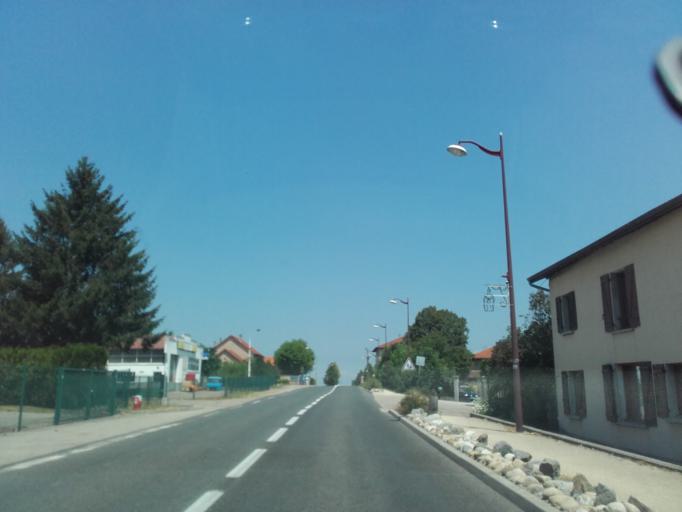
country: FR
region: Rhone-Alpes
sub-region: Departement de l'Isere
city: Nivolas-Vermelle
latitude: 45.5066
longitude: 5.3029
